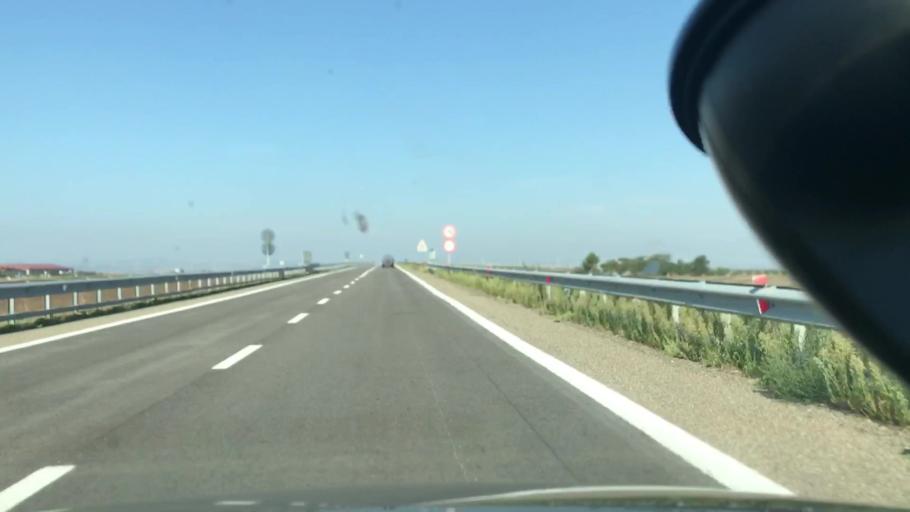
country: IT
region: Basilicate
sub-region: Provincia di Potenza
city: Montemilone
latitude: 40.9923
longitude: 15.8934
